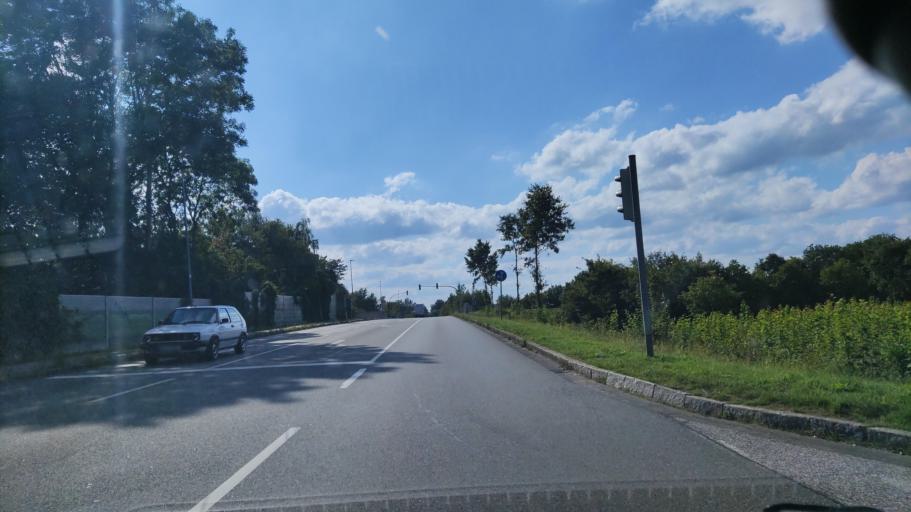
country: DE
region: Schleswig-Holstein
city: Fockbek
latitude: 54.3174
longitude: 9.6239
